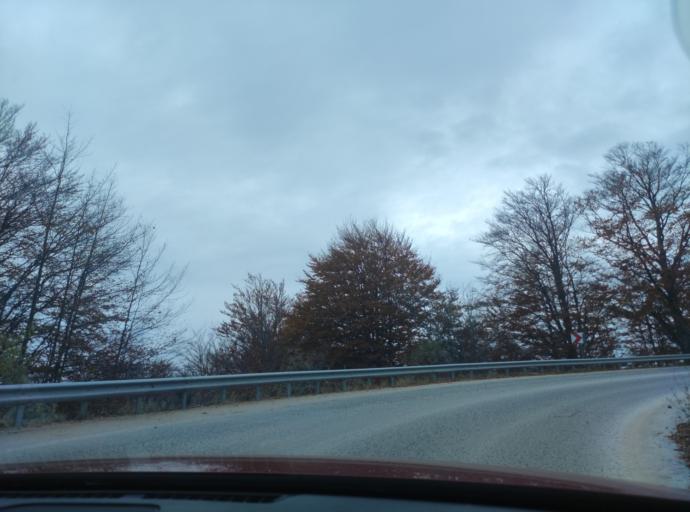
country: BG
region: Sofiya
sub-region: Obshtina Godech
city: Godech
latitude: 43.1128
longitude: 23.1104
